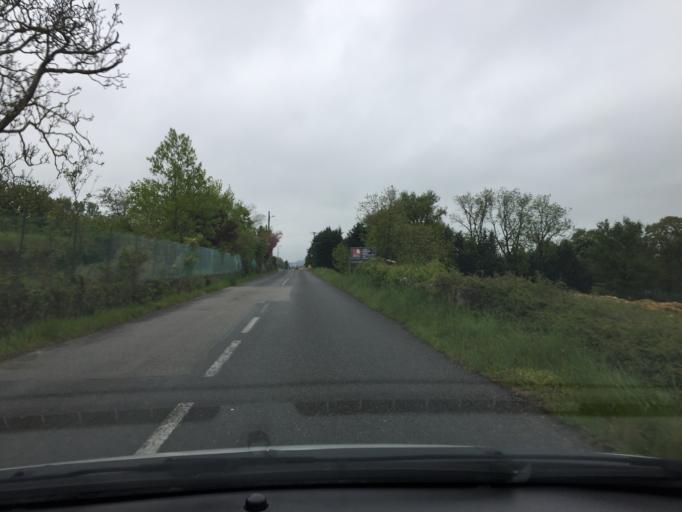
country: FR
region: Rhone-Alpes
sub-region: Departement du Rhone
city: Mornant
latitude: 45.6180
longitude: 4.6889
